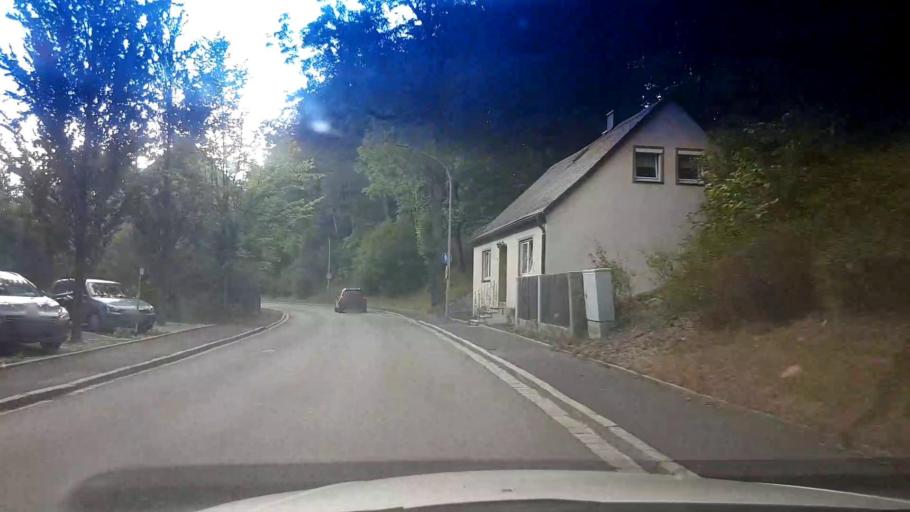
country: DE
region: Bavaria
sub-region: Upper Palatinate
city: Tirschenreuth
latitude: 49.8813
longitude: 12.3361
